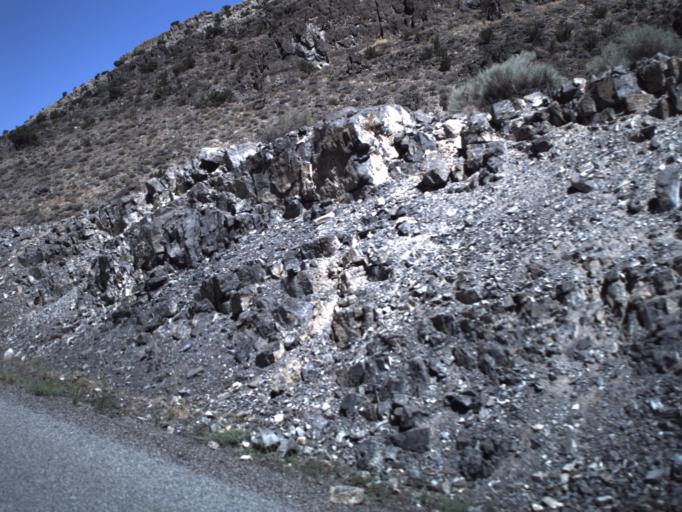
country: US
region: Utah
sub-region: Beaver County
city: Milford
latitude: 39.0831
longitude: -113.5915
